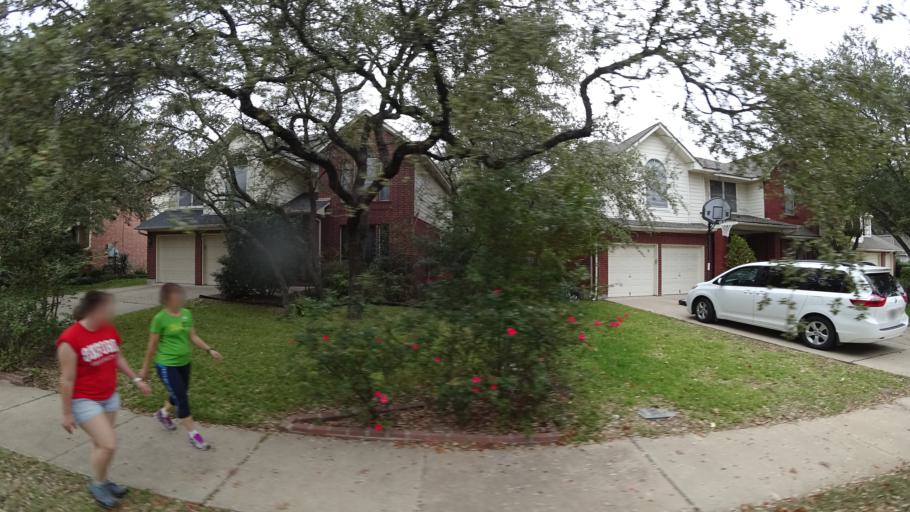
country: US
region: Texas
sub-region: Williamson County
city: Anderson Mill
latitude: 30.4369
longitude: -97.8284
